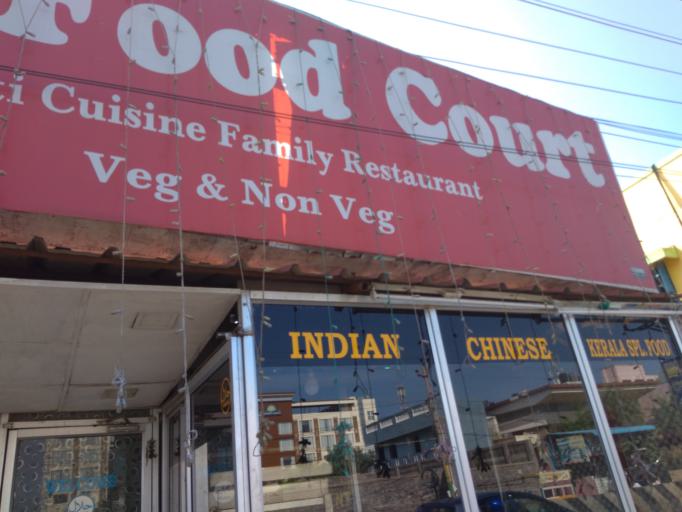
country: IN
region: Tamil Nadu
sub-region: Kancheepuram
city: Vengavasal
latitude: 12.8034
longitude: 80.2238
